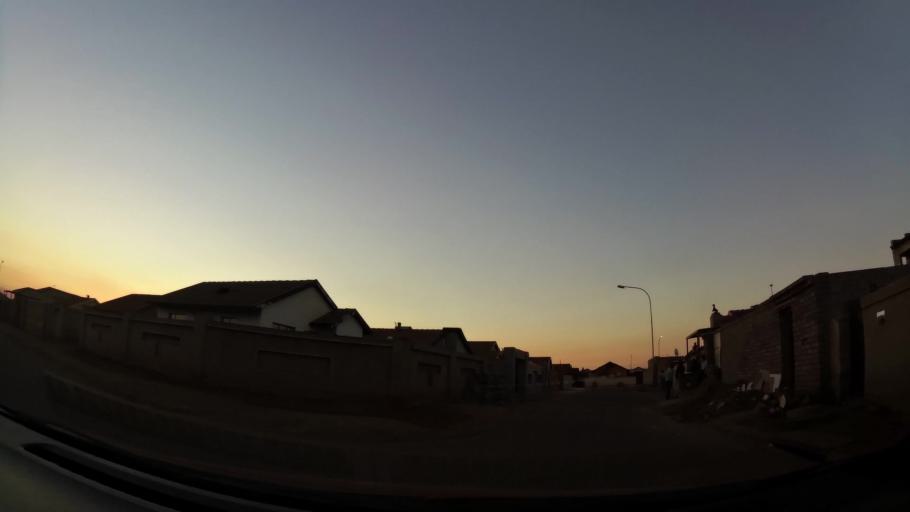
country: ZA
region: Gauteng
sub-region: City of Johannesburg Metropolitan Municipality
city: Soweto
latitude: -26.2302
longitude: 27.8400
